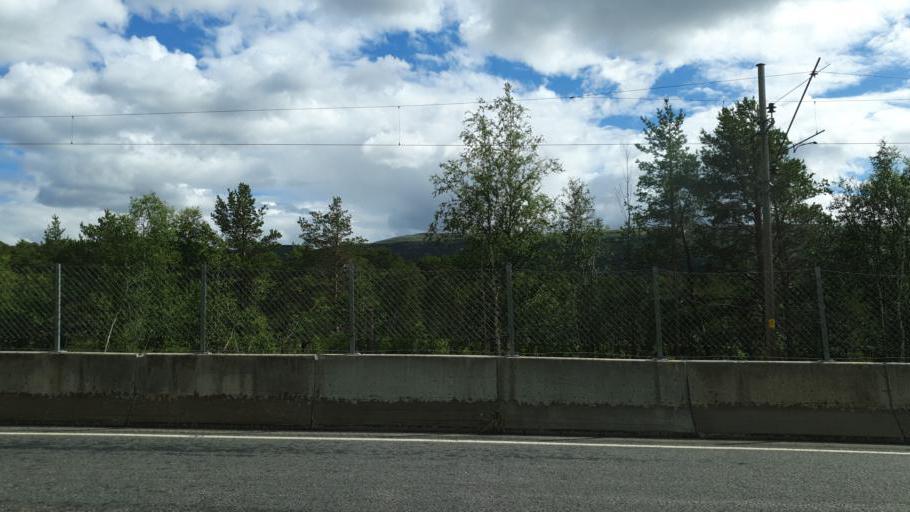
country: NO
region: Sor-Trondelag
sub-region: Oppdal
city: Oppdal
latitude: 62.6127
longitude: 9.7502
